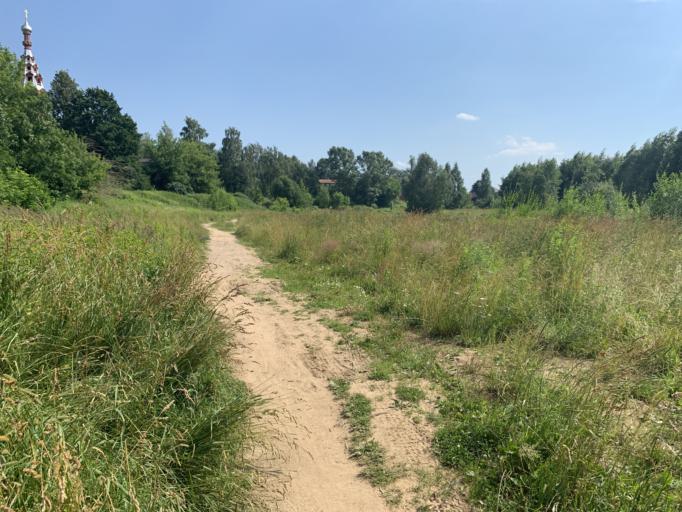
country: RU
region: Moskovskaya
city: Cherkizovo
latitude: 55.9714
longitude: 37.7955
